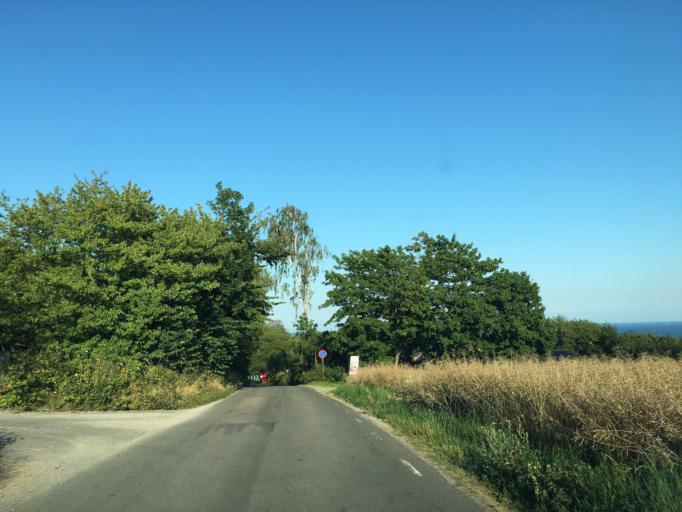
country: SE
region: Skane
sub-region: Simrishamns Kommun
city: Kivik
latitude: 55.6592
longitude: 14.2589
